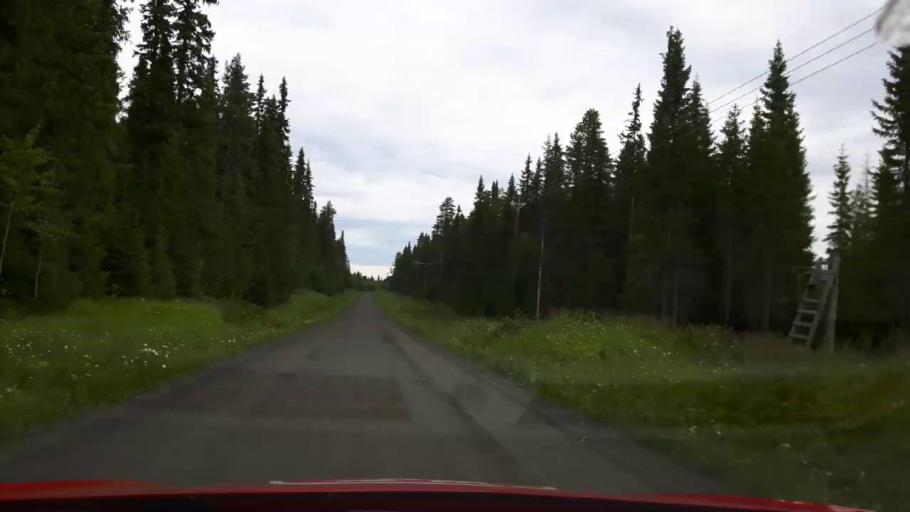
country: SE
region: Jaemtland
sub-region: Stroemsunds Kommun
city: Stroemsund
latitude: 63.4652
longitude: 15.2851
